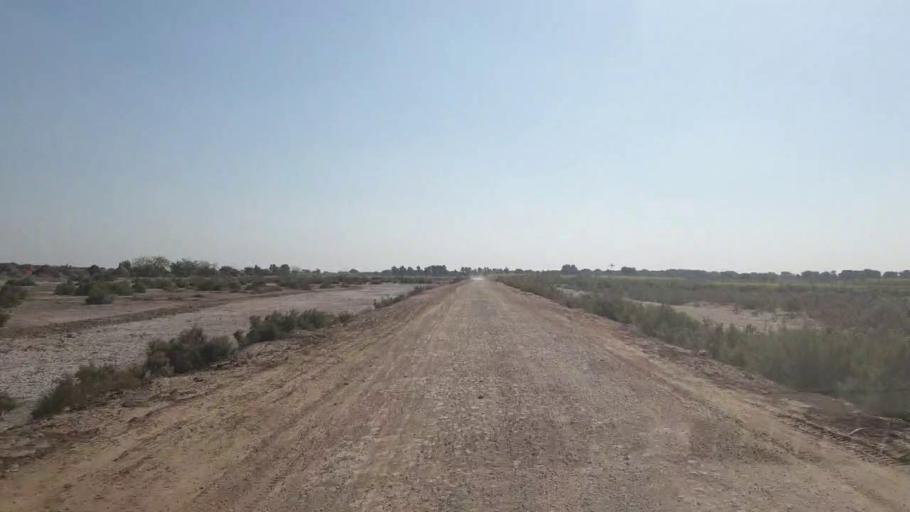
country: PK
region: Sindh
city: Chambar
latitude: 25.3223
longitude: 68.7398
